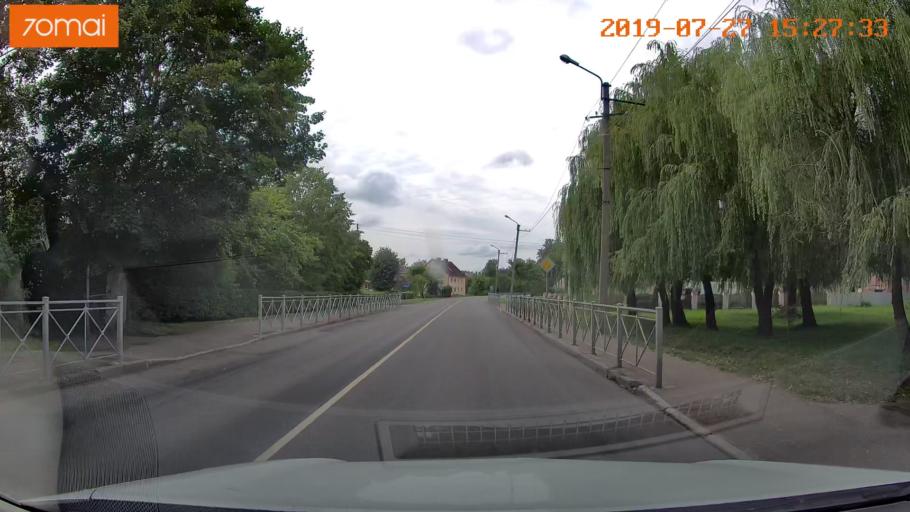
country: RU
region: Kaliningrad
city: Nesterov
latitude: 54.6340
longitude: 22.5626
